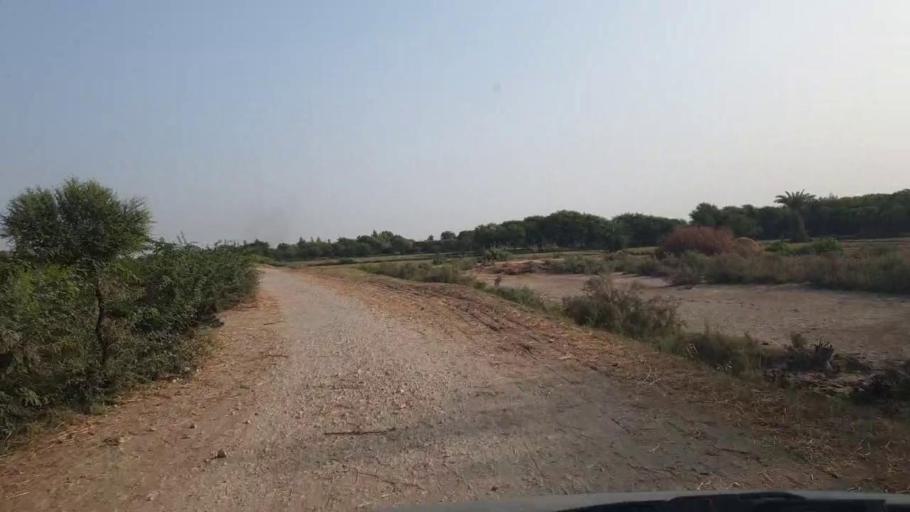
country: PK
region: Sindh
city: Rajo Khanani
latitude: 25.0385
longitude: 68.7695
